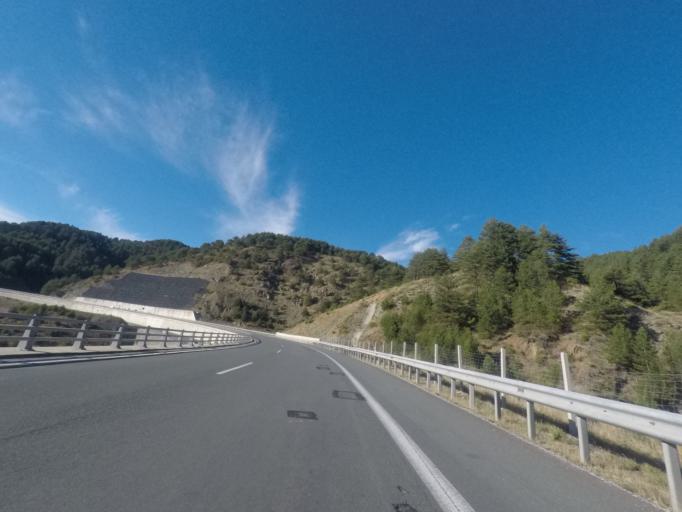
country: GR
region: Epirus
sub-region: Nomos Ioanninon
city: Metsovo
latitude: 39.7893
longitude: 21.2799
